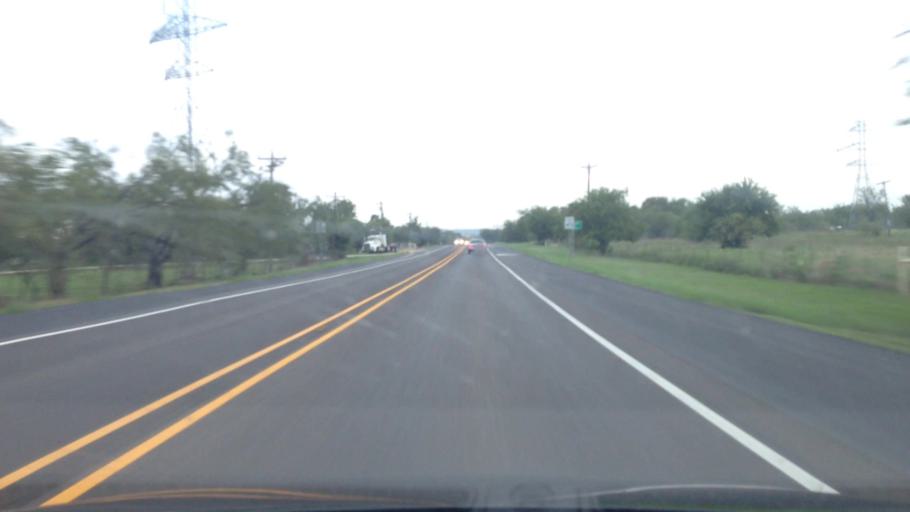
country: US
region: Texas
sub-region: Johnson County
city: Burleson
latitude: 32.5072
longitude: -97.3459
